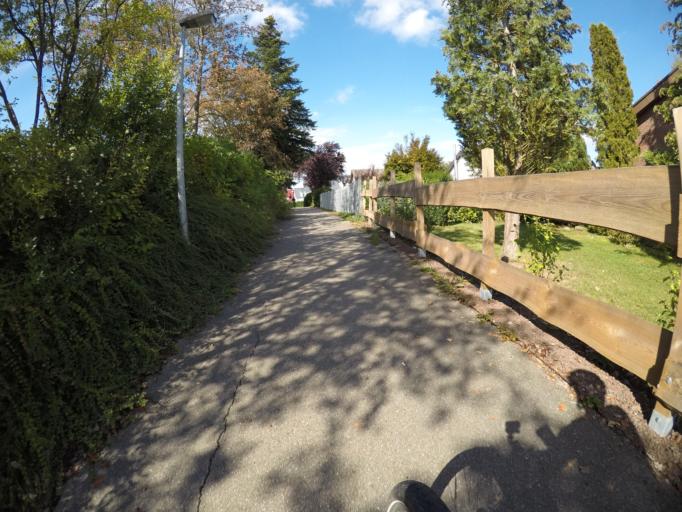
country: DE
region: Baden-Wuerttemberg
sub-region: Regierungsbezirk Stuttgart
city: Gartringen
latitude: 48.6379
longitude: 8.8940
